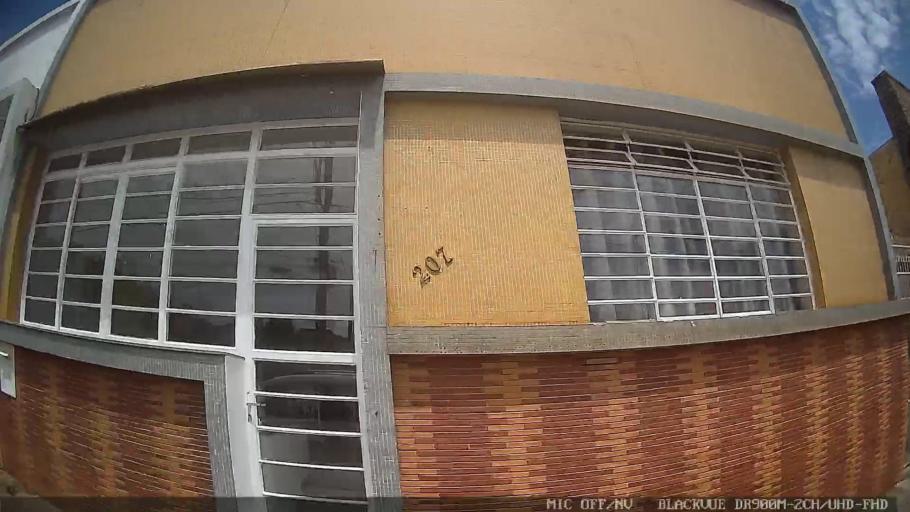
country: BR
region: Sao Paulo
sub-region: Laranjal Paulista
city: Laranjal Paulista
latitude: -23.0482
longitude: -47.8368
